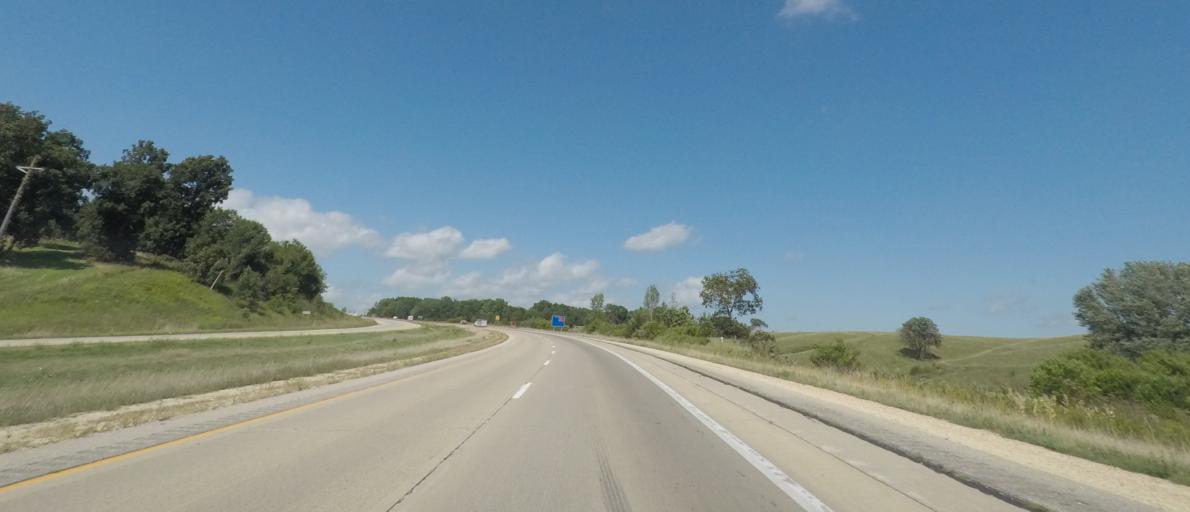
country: US
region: Iowa
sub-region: Jones County
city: Anamosa
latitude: 42.0870
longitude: -91.2683
